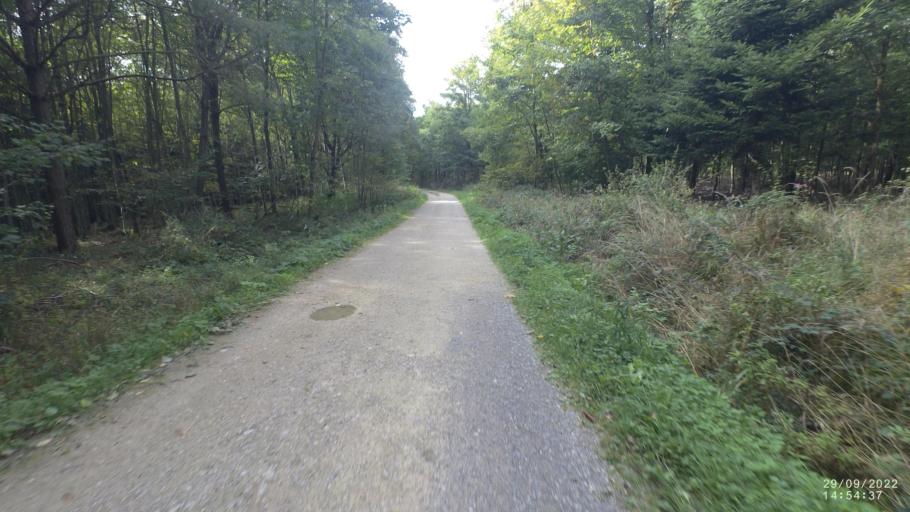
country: DE
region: Baden-Wuerttemberg
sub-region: Regierungsbezirk Stuttgart
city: Adelberg
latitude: 48.7757
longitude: 9.5744
